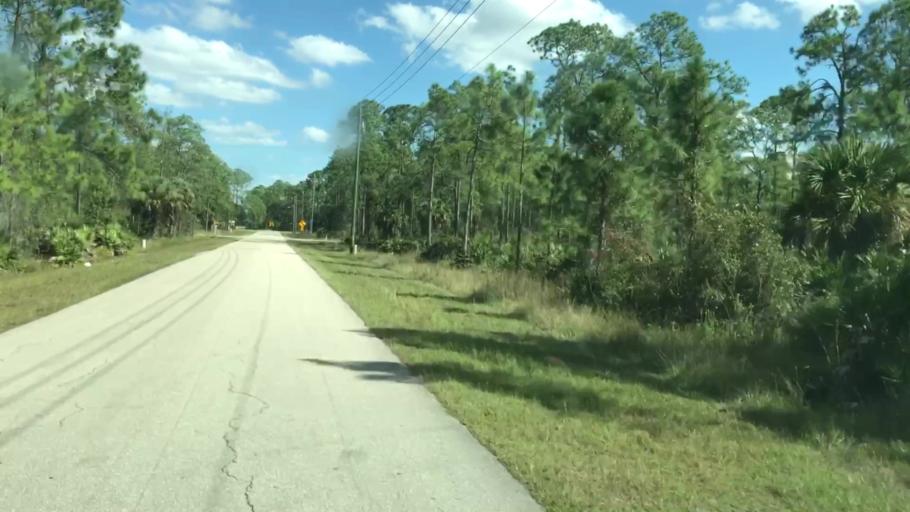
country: US
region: Florida
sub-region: Lee County
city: Alva
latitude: 26.6836
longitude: -81.5852
